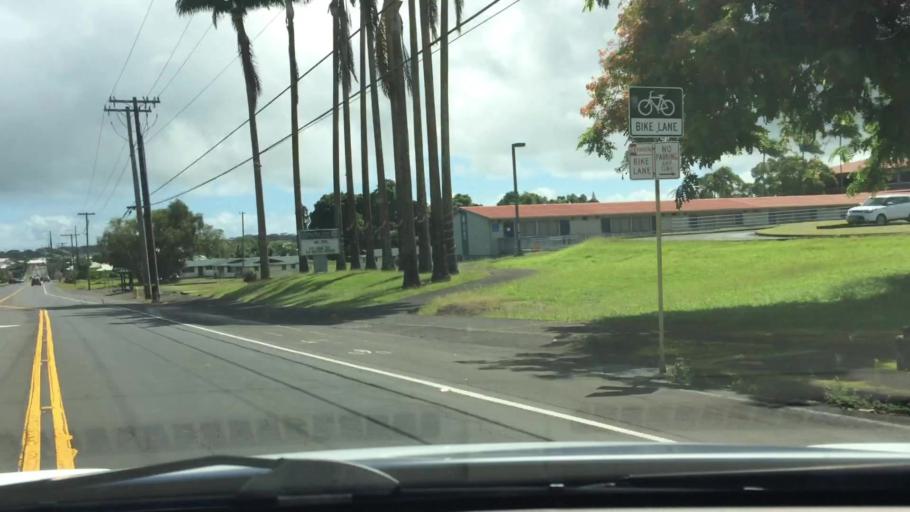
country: US
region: Hawaii
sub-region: Hawaii County
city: Hilo
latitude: 19.7010
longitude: -155.0772
